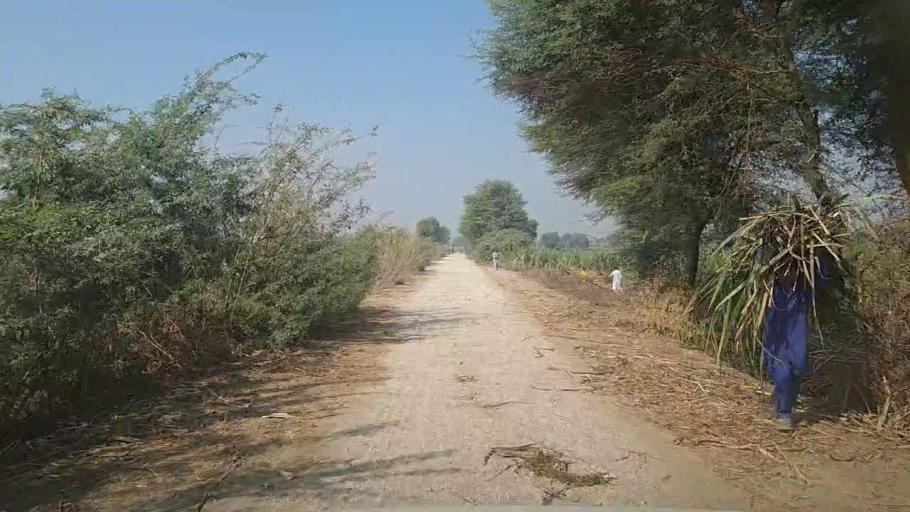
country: PK
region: Sindh
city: Karaundi
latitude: 26.9731
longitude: 68.4522
